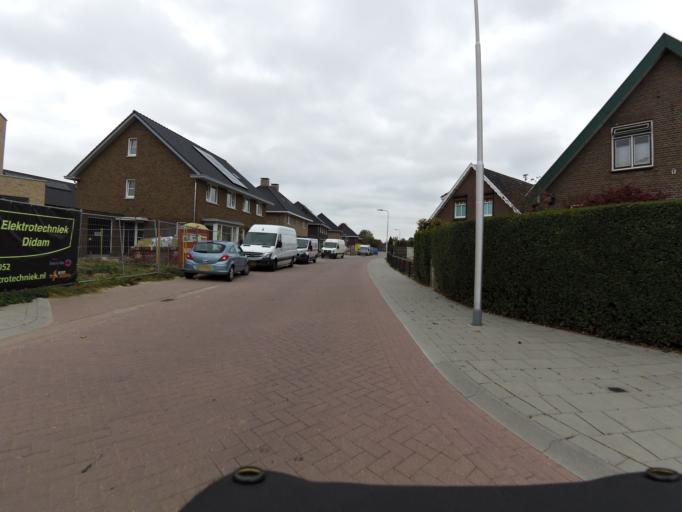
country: NL
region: Gelderland
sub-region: Gemeente Zevenaar
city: Zevenaar
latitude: 51.8897
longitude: 6.0448
